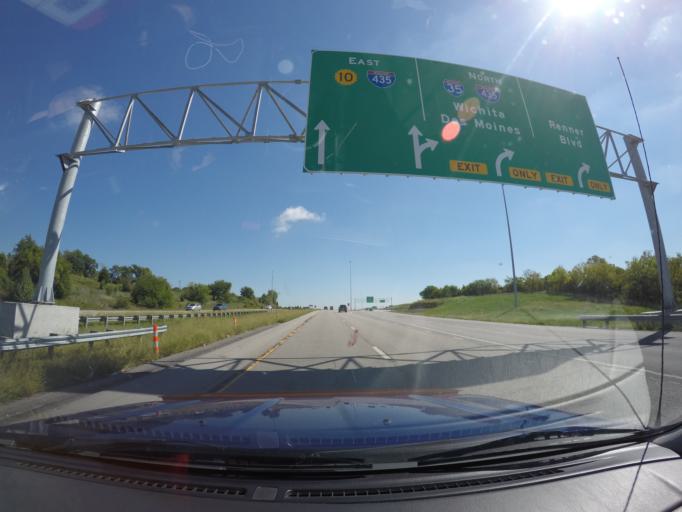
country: US
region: Kansas
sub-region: Johnson County
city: Lenexa
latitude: 38.9415
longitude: -94.7885
